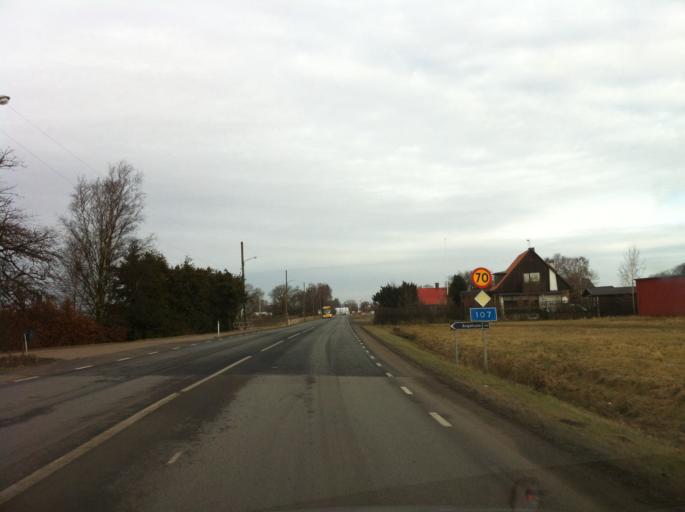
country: SE
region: Skane
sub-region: Angelholms Kommun
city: Strovelstorp
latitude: 56.1783
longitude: 12.8447
